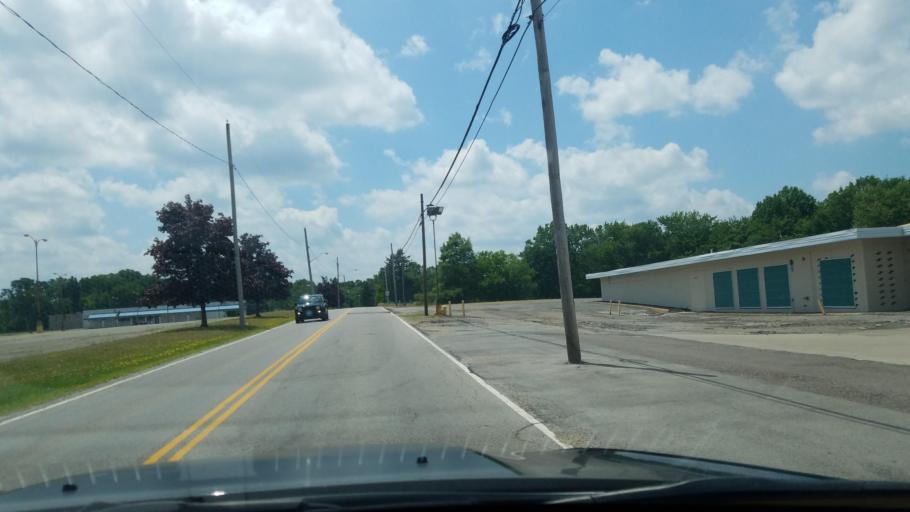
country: US
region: Ohio
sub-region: Trumbull County
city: Bolindale
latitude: 41.2195
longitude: -80.7798
